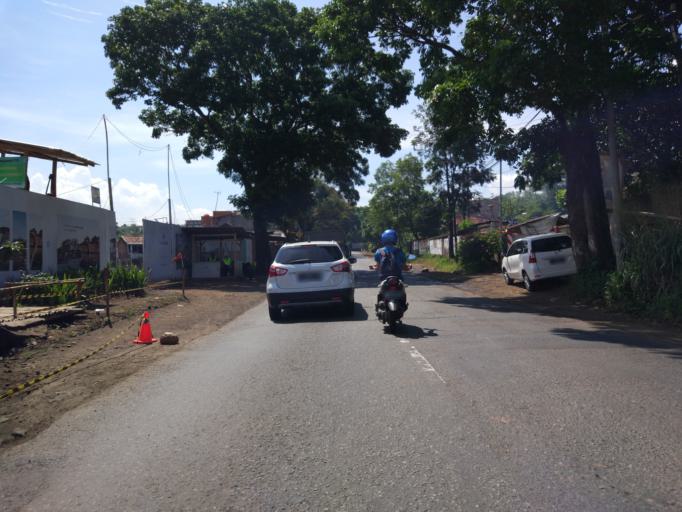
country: ID
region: West Java
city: Cileunyi
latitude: -6.9231
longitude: 107.7866
